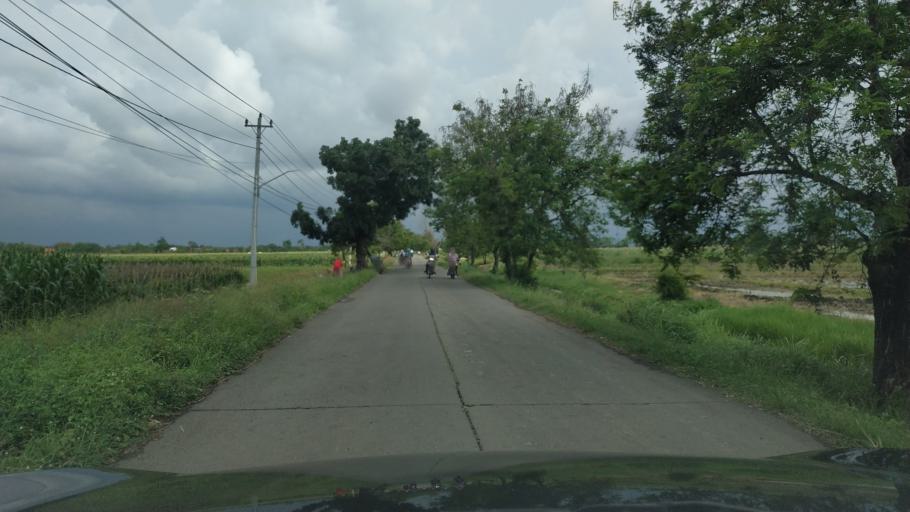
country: ID
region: Central Java
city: Pemalang
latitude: -6.9025
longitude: 109.3257
